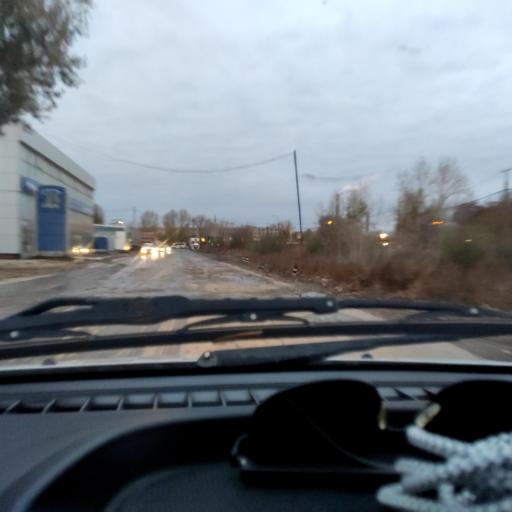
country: RU
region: Samara
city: Zhigulevsk
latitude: 53.4775
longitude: 49.4970
